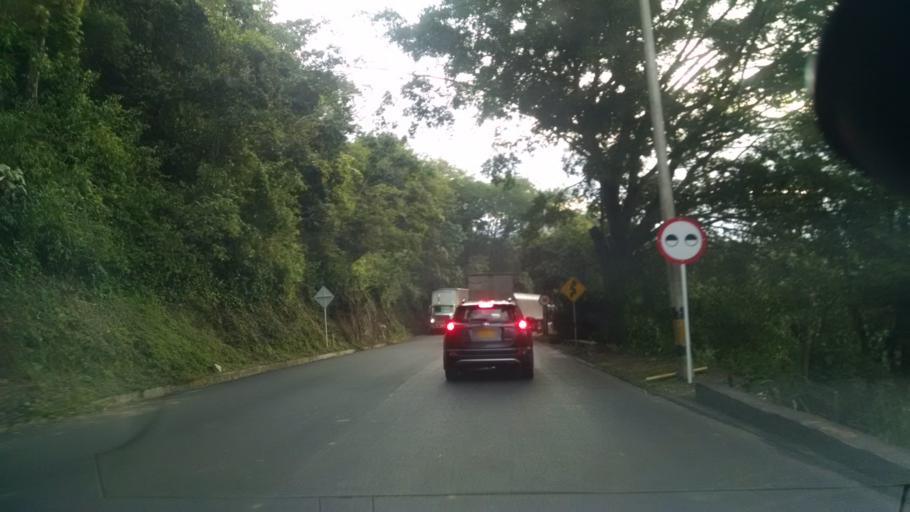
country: CO
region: Antioquia
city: Santa Barbara
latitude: 5.8458
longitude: -75.5782
